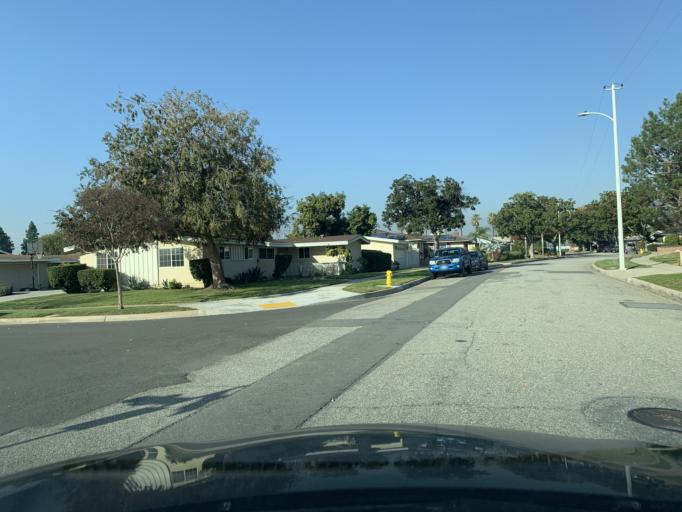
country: US
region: California
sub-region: Los Angeles County
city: Covina
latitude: 34.0803
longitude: -117.8971
